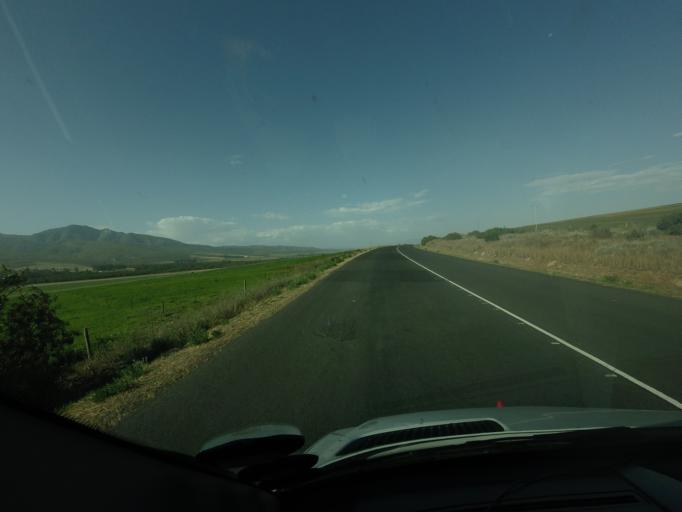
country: ZA
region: Western Cape
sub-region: Cape Winelands District Municipality
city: Ashton
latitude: -34.1466
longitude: 19.9807
